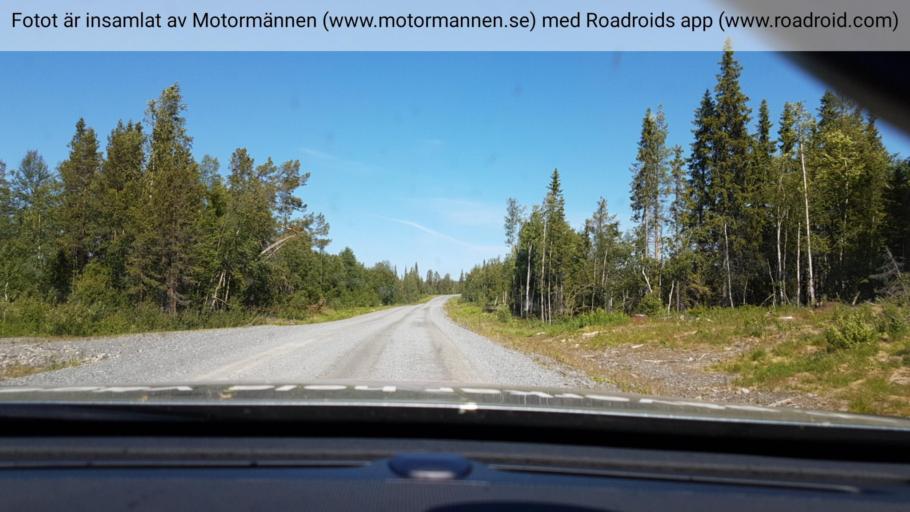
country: SE
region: Vaesterbotten
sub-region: Vilhelmina Kommun
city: Sjoberg
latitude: 64.6974
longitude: 15.7576
